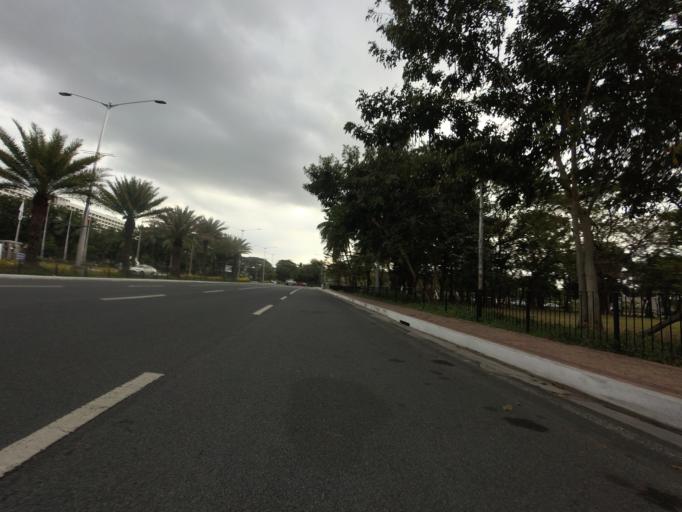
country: PH
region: Metro Manila
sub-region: City of Manila
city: Port Area
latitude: 14.5554
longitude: 120.9817
